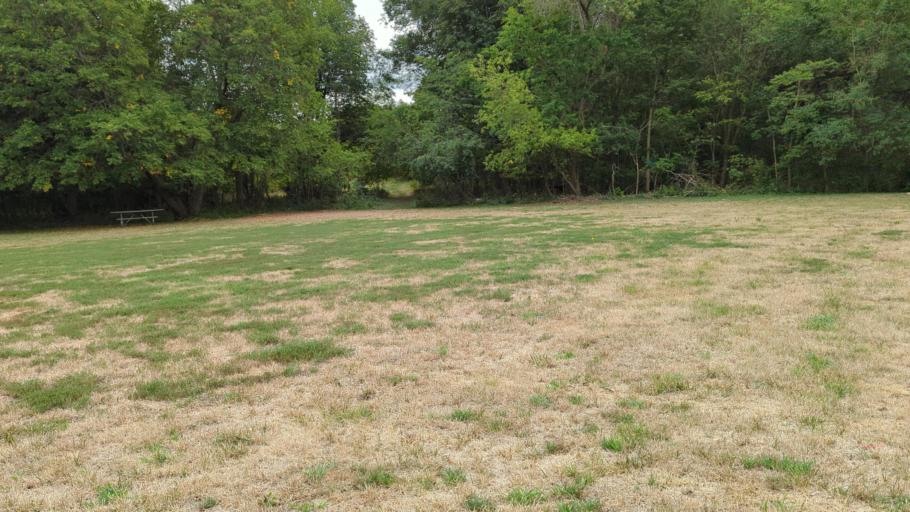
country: US
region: South Dakota
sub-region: Union County
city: Beresford
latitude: 42.9249
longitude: -96.7800
